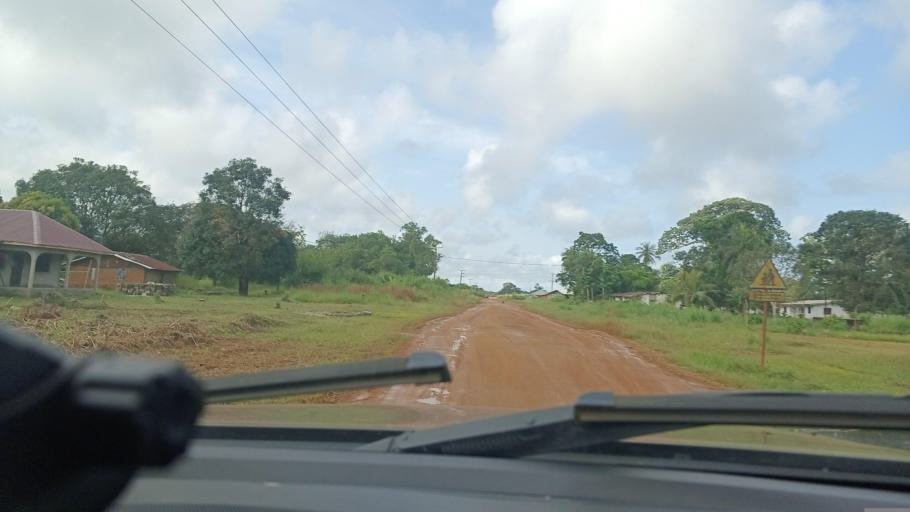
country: LR
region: Grand Cape Mount
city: Robertsport
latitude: 6.6879
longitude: -11.1182
